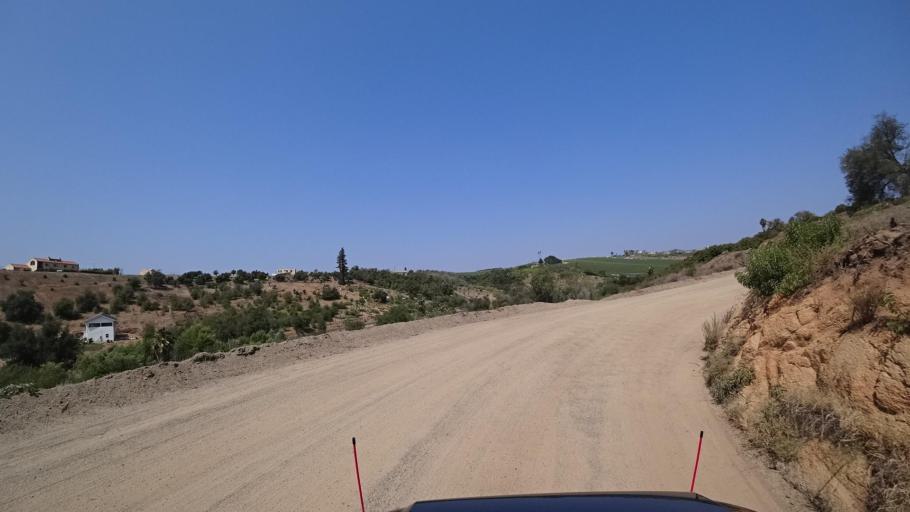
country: US
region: California
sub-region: San Diego County
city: Bonsall
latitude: 33.2791
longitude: -117.2464
